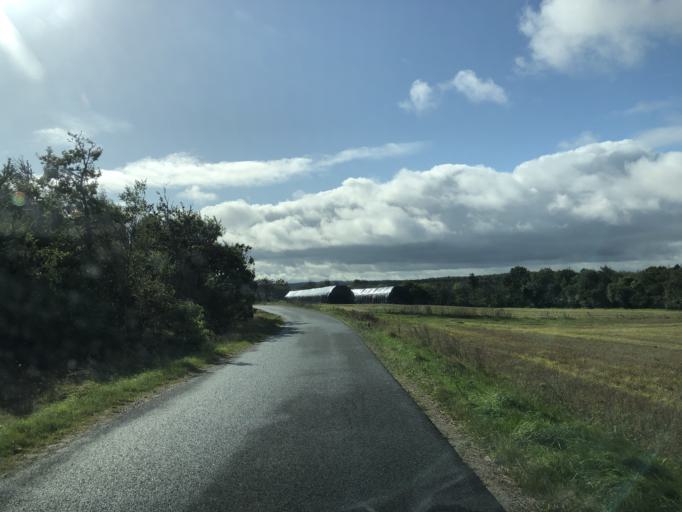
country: DK
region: Central Jutland
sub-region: Holstebro Kommune
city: Ulfborg
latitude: 56.2972
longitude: 8.4604
